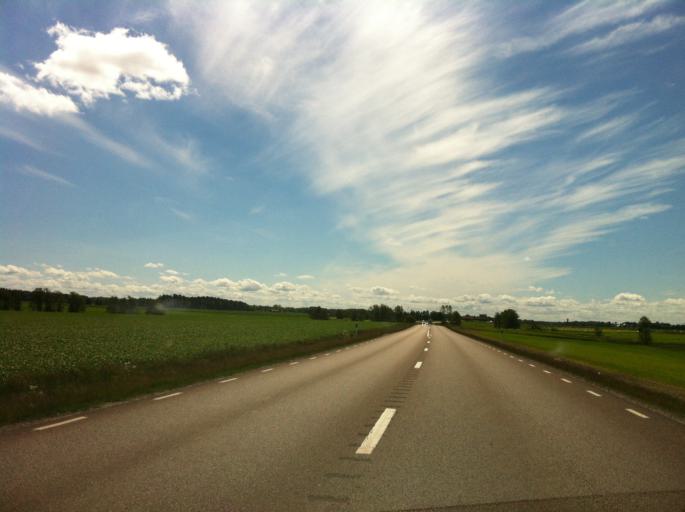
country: SE
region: Vaestra Goetaland
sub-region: Vanersborgs Kommun
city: Bralanda
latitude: 58.5330
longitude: 12.3194
